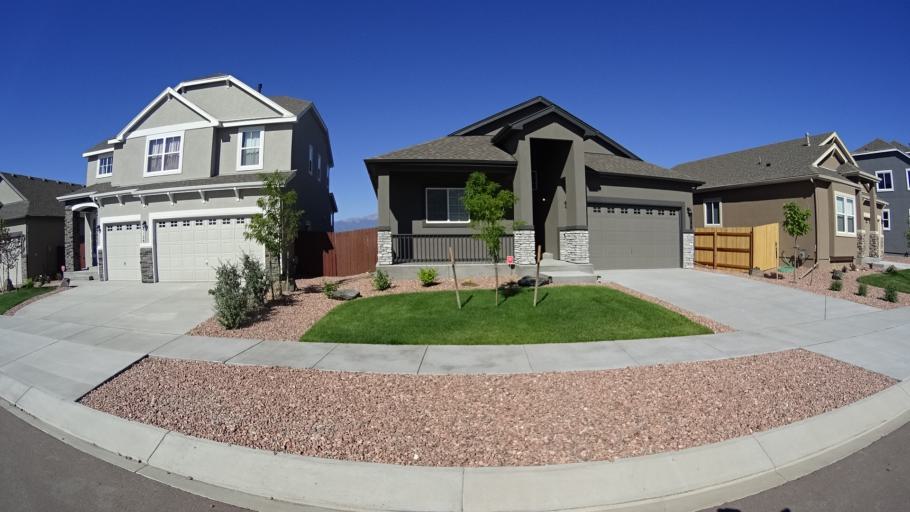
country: US
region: Colorado
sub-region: El Paso County
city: Black Forest
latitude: 38.9505
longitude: -104.6760
